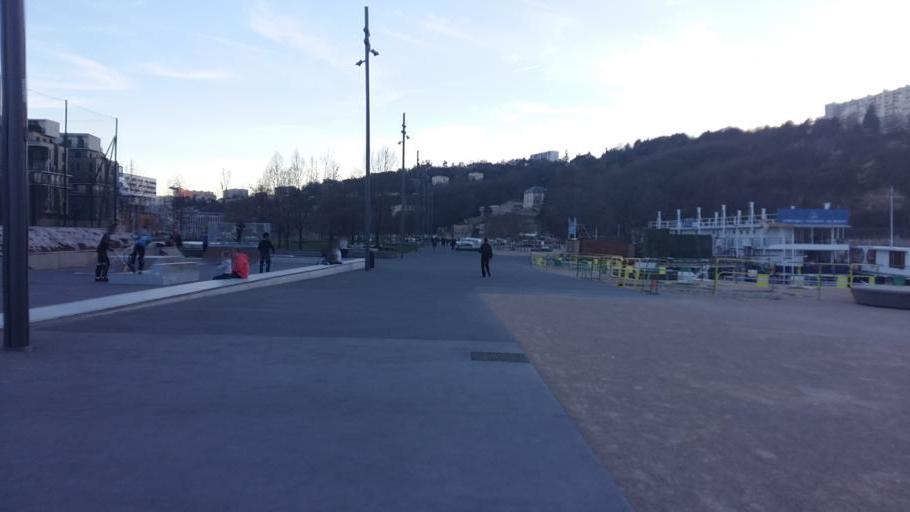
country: FR
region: Rhone-Alpes
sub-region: Departement du Rhone
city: Sainte-Foy-les-Lyon
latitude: 45.7454
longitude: 4.8161
